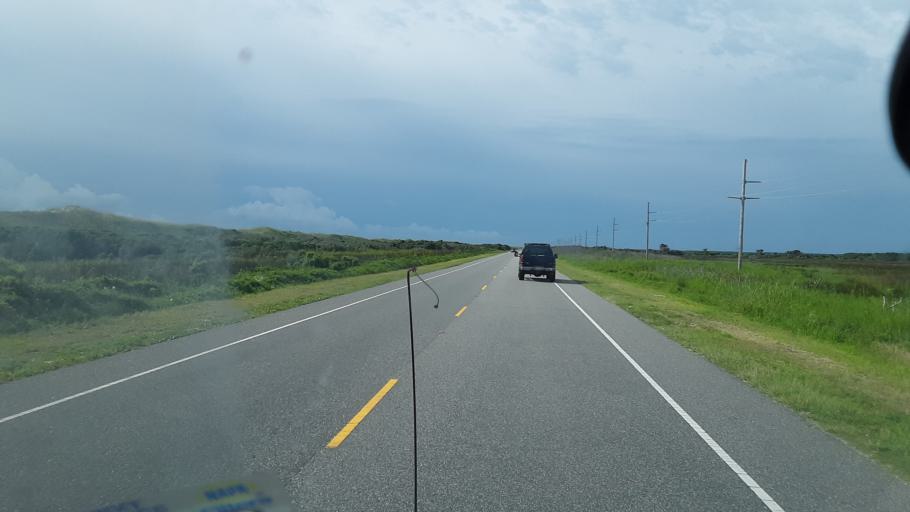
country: US
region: North Carolina
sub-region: Dare County
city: Buxton
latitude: 35.3133
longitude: -75.5114
